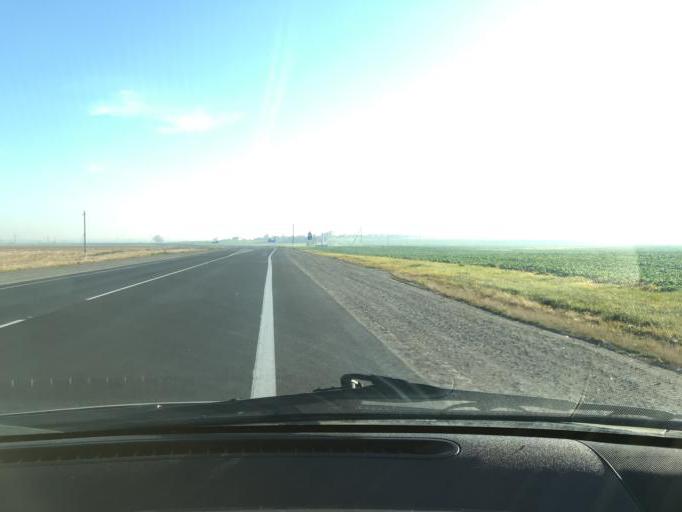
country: BY
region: Brest
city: Asnyezhytsy
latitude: 52.1878
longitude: 26.0927
